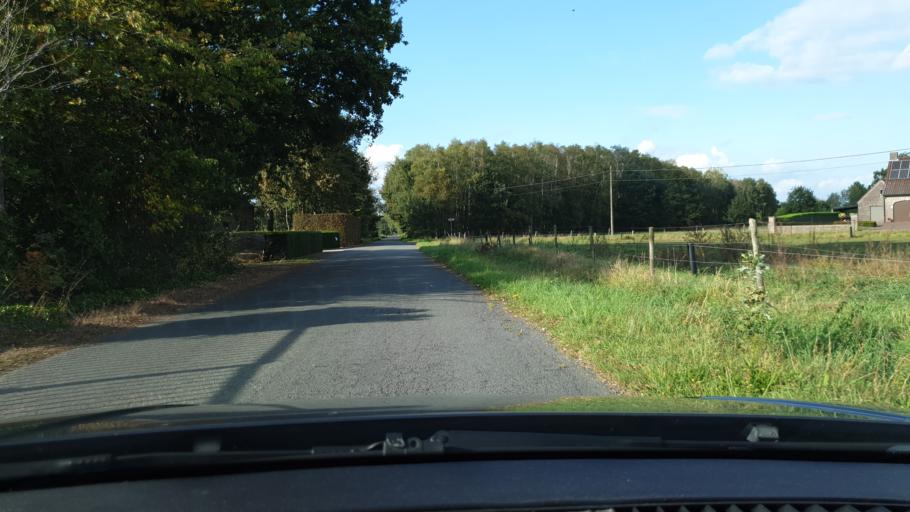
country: BE
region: Flanders
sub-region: Provincie Antwerpen
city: Geel
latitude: 51.1950
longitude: 5.0223
